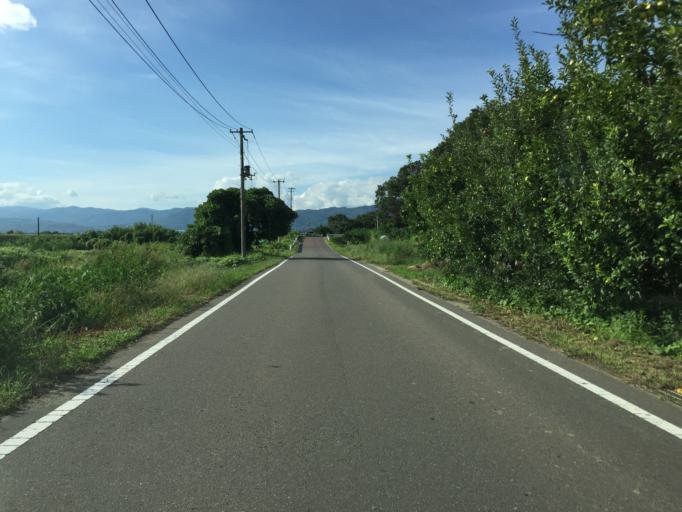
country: JP
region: Fukushima
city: Hobaramachi
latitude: 37.8072
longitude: 140.5092
